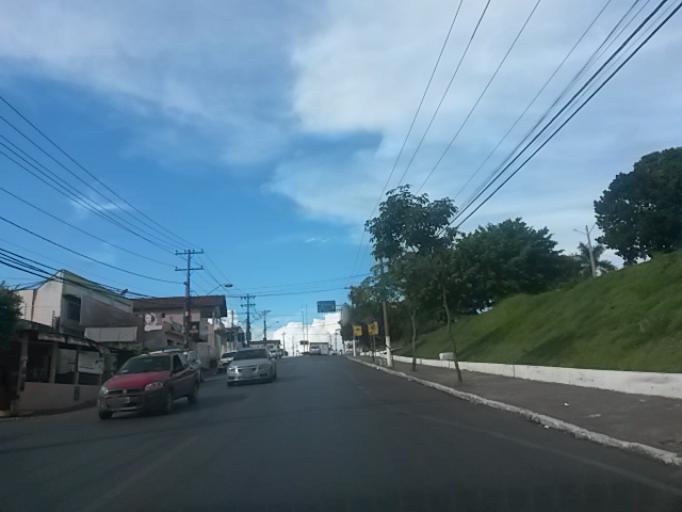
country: BR
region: Mato Grosso
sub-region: Cuiaba
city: Cuiaba
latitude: -15.5962
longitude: -56.0798
